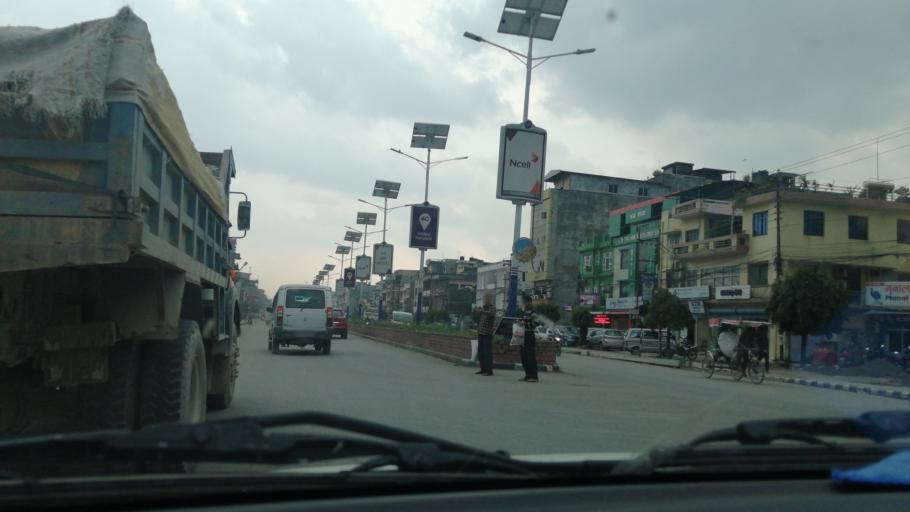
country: NP
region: Western Region
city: Butwal
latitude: 27.7051
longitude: 83.4672
